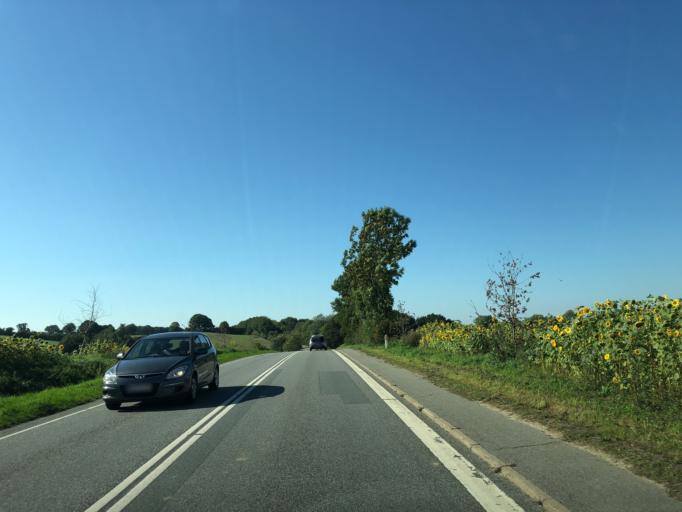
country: DK
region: South Denmark
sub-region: Aabenraa Kommune
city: Aabenraa
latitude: 55.0154
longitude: 9.4741
